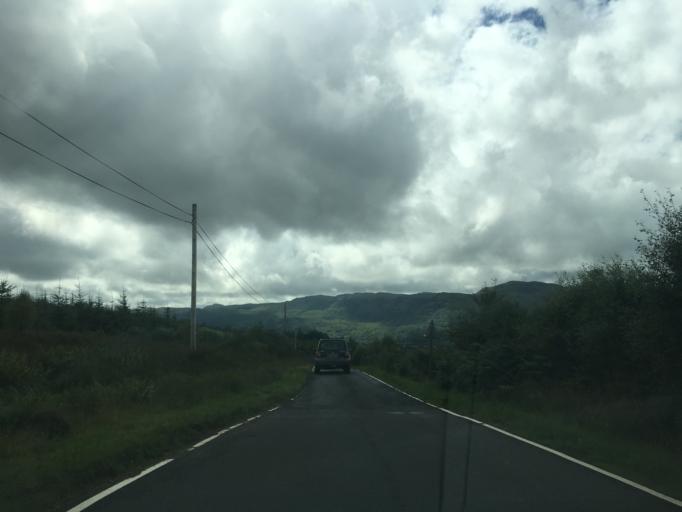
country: GB
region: Scotland
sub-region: Argyll and Bute
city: Port Bannatyne
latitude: 55.9911
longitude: -5.1496
